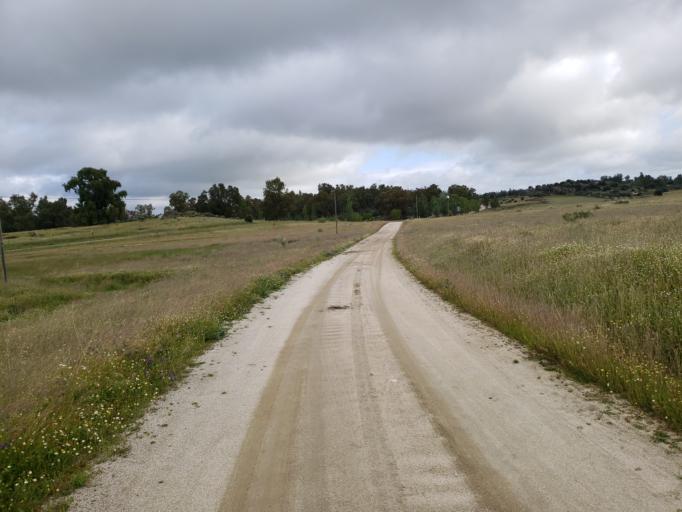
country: ES
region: Extremadura
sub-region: Provincia de Caceres
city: Malpartida de Caceres
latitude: 39.4261
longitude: -6.5039
